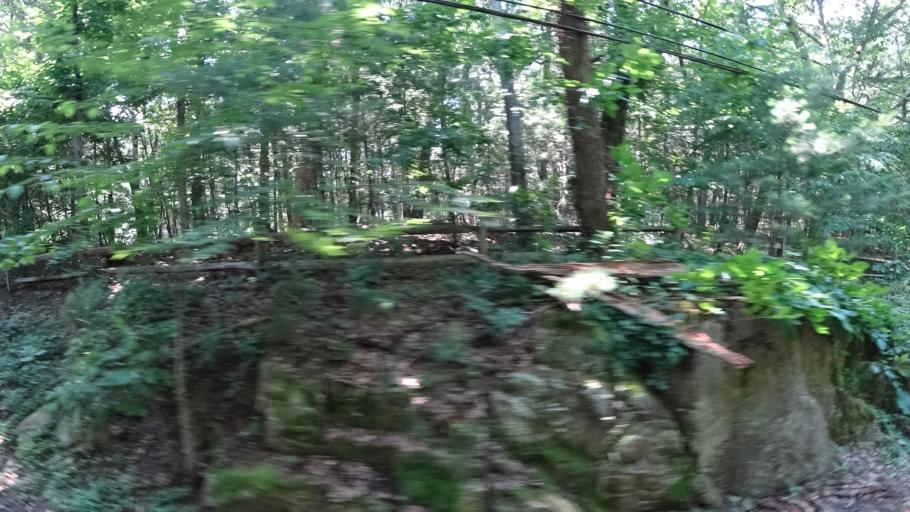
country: US
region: Massachusetts
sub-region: Norfolk County
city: Dedham
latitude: 42.2500
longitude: -71.1976
